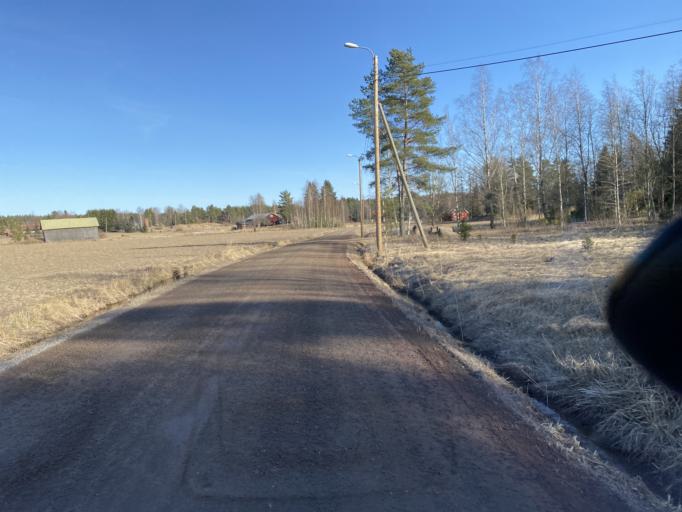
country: FI
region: Satakunta
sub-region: Rauma
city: Lappi
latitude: 61.1403
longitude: 21.9445
